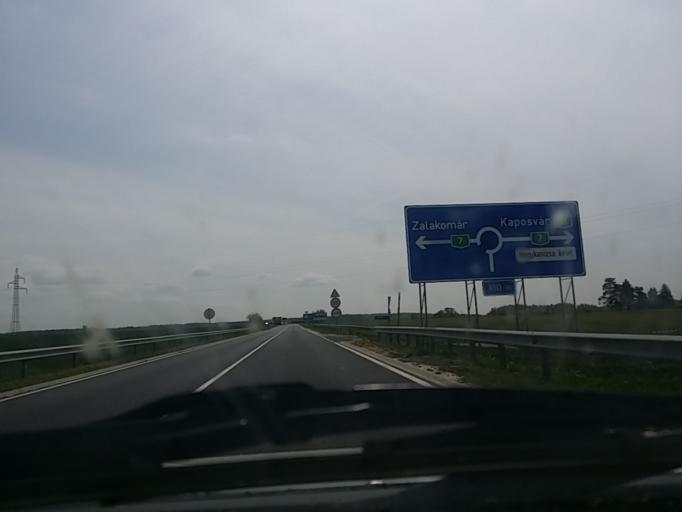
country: HU
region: Zala
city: Nagykanizsa
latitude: 46.4718
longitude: 17.0327
